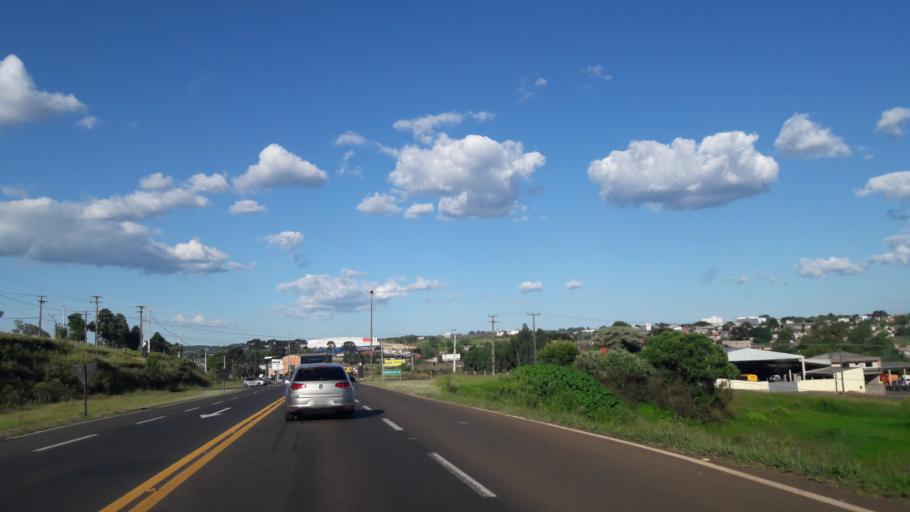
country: BR
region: Parana
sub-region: Guarapuava
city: Guarapuava
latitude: -25.3683
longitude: -51.4947
